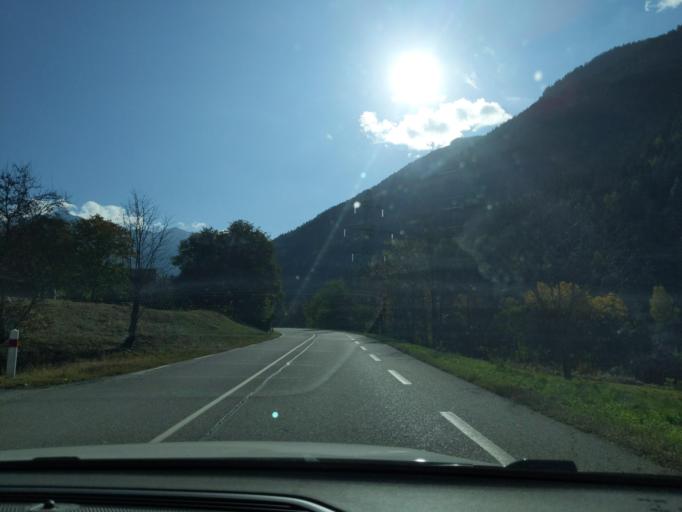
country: FR
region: Rhone-Alpes
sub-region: Departement de la Savoie
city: Seez
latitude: 45.6141
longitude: 6.8233
